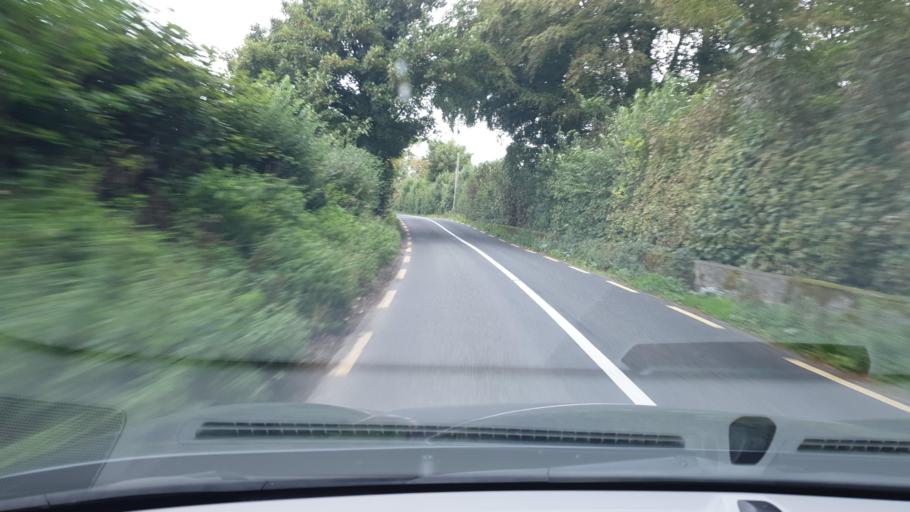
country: IE
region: Leinster
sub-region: Kildare
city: Kilcock
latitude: 53.4117
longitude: -6.6611
